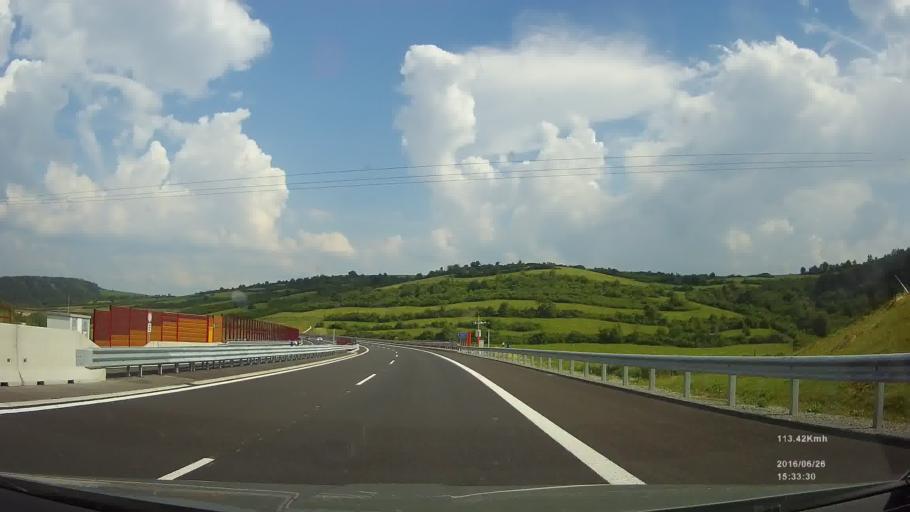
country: SK
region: Presovsky
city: Sabinov
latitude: 49.0005
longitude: 21.0583
